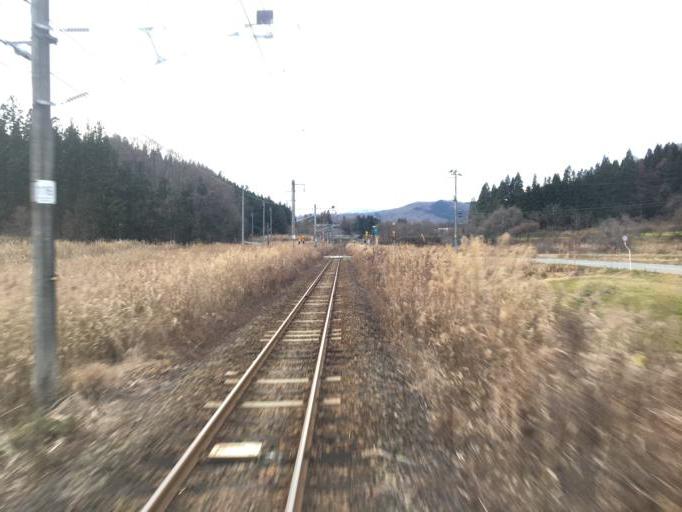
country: JP
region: Yamagata
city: Shinjo
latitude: 38.8308
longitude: 140.2497
